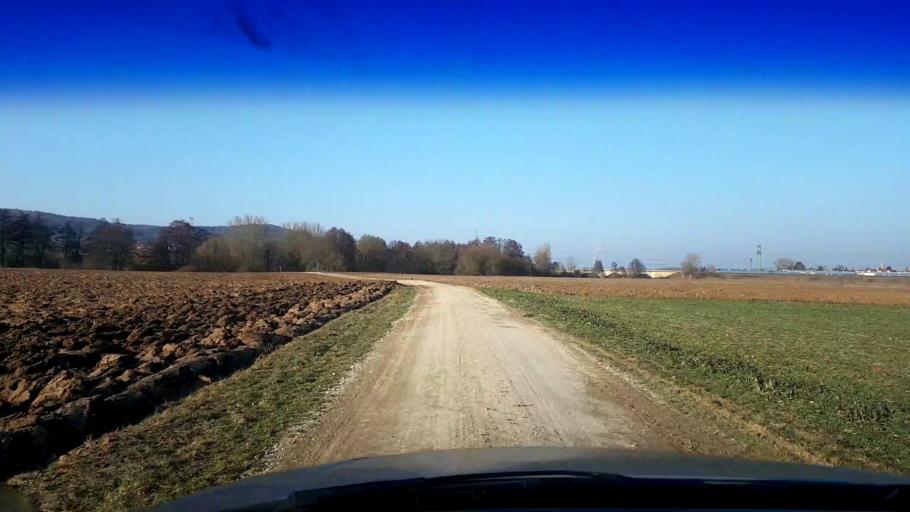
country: DE
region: Bavaria
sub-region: Upper Franconia
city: Hallstadt
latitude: 49.9201
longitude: 10.8600
